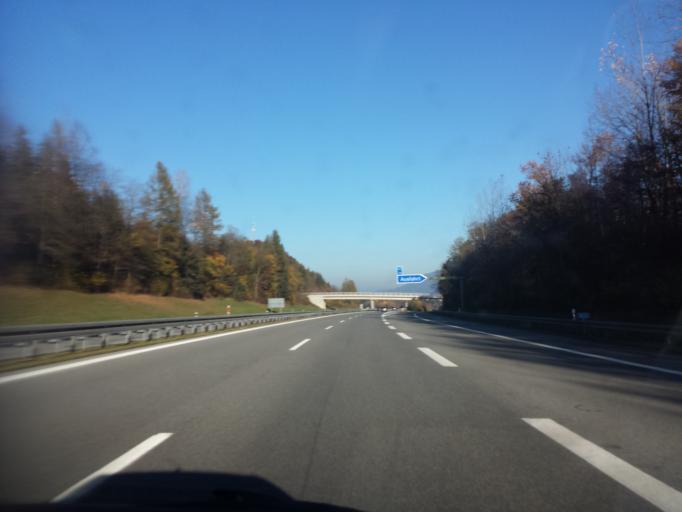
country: DE
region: Bavaria
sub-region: Upper Bavaria
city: Grossweil
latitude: 47.6706
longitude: 11.2740
